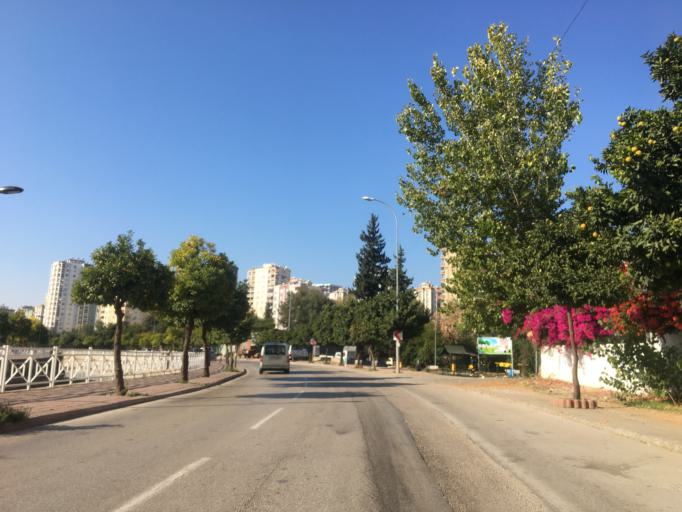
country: TR
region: Adana
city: Seyhan
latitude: 37.0297
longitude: 35.2824
